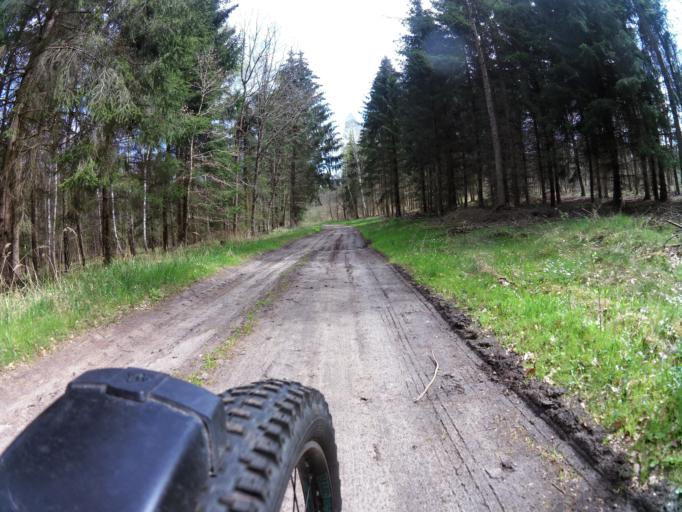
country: PL
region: West Pomeranian Voivodeship
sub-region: Powiat lobeski
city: Resko
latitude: 53.7545
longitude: 15.3524
